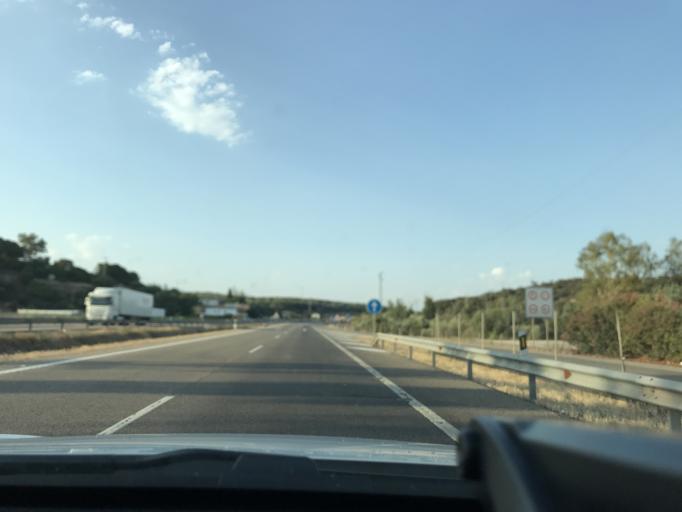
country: ES
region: Andalusia
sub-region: Provincia de Jaen
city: Espeluy
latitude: 38.0797
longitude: -3.8460
